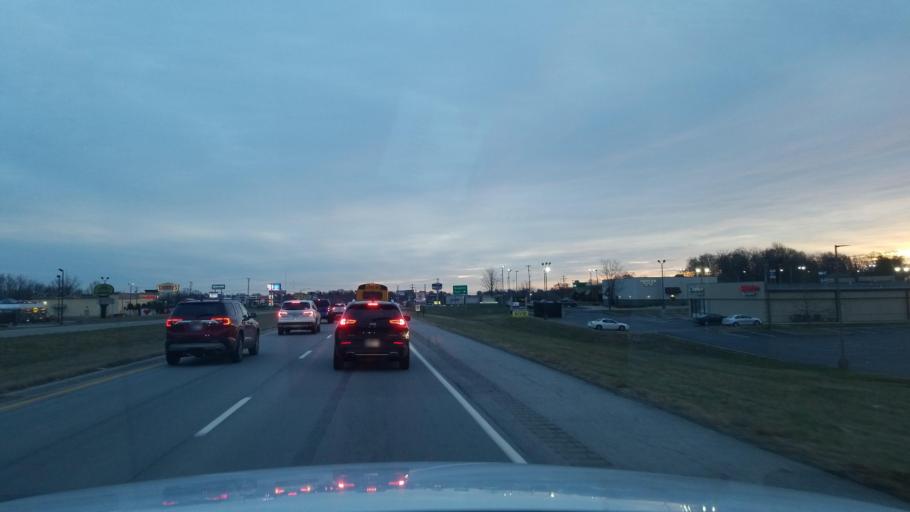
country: US
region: Indiana
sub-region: Vanderburgh County
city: Evansville
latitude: 37.9758
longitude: -87.6405
